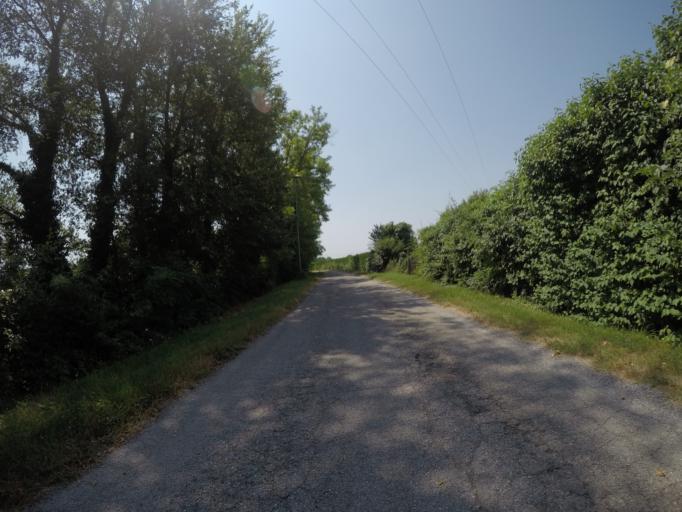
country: IT
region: Veneto
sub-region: Provincia di Rovigo
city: Pincara
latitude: 45.0064
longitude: 11.6419
